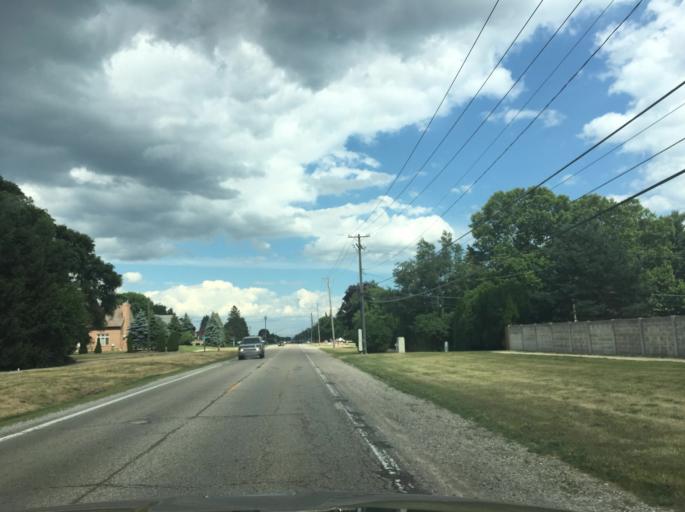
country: US
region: Michigan
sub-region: Macomb County
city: Utica
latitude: 42.6411
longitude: -82.9993
